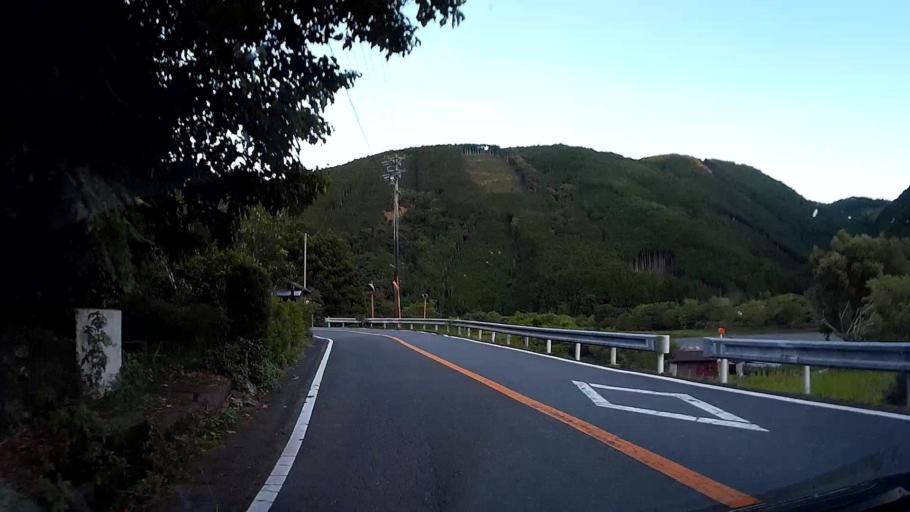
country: JP
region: Shizuoka
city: Shizuoka-shi
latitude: 35.1098
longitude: 138.3428
